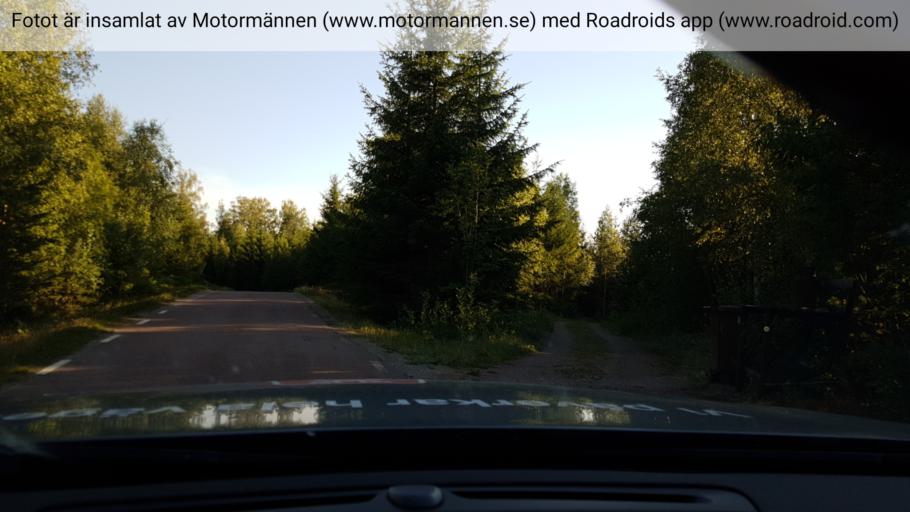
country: SE
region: Vaestmanland
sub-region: Surahammars Kommun
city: Surahammar
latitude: 59.6556
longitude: 16.0741
